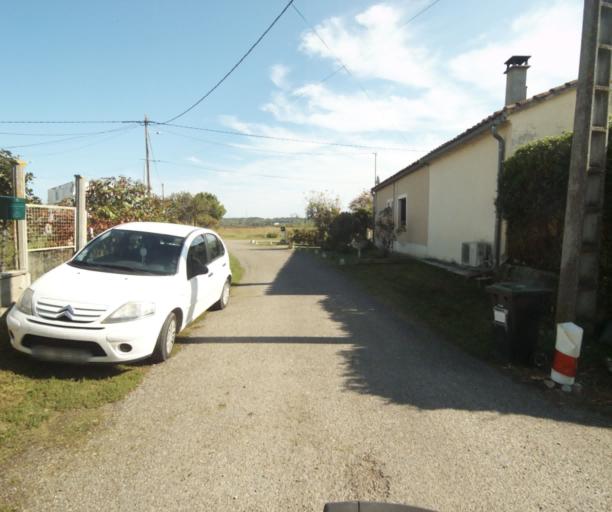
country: FR
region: Midi-Pyrenees
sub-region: Departement du Tarn-et-Garonne
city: Verdun-sur-Garonne
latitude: 43.8648
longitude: 1.2454
